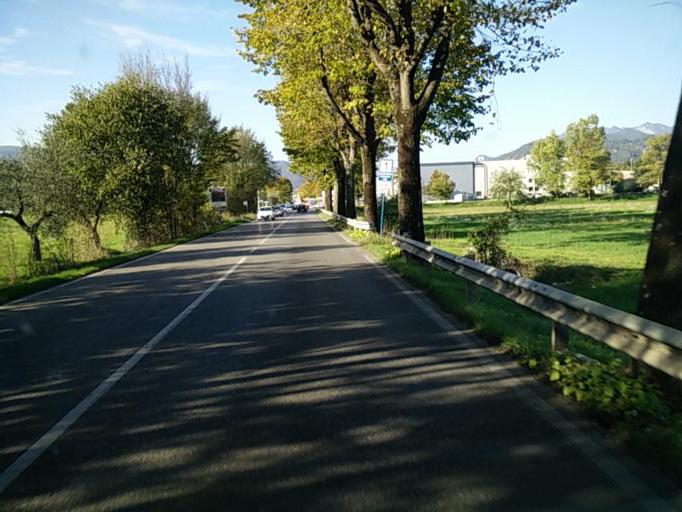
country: IT
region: Lombardy
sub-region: Provincia di Brescia
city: Cunettone-Villa
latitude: 45.5803
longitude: 10.5228
